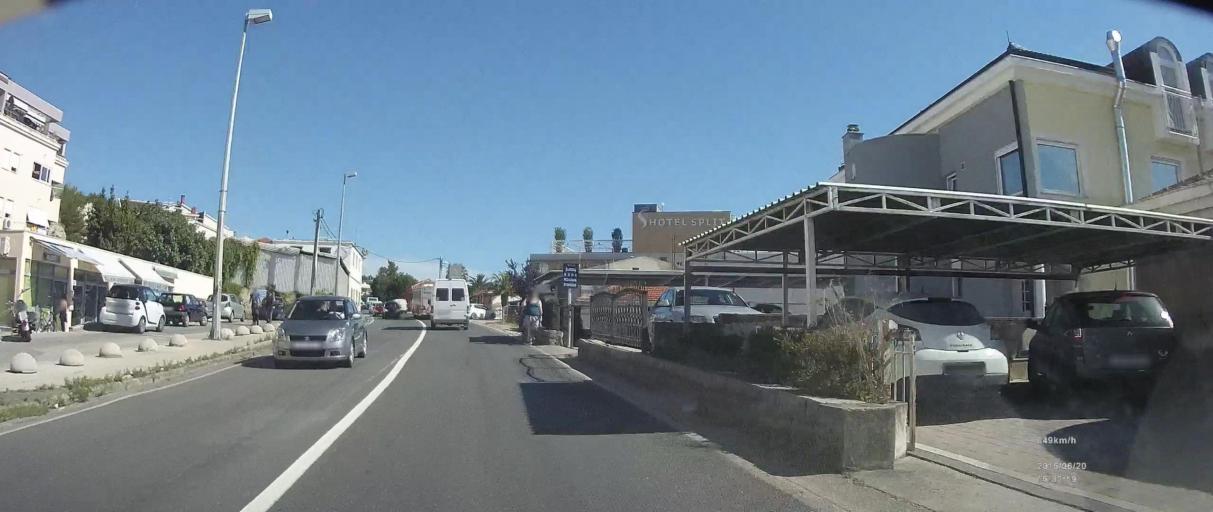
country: HR
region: Splitsko-Dalmatinska
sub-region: Grad Split
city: Stobrec
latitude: 43.4989
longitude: 16.5358
